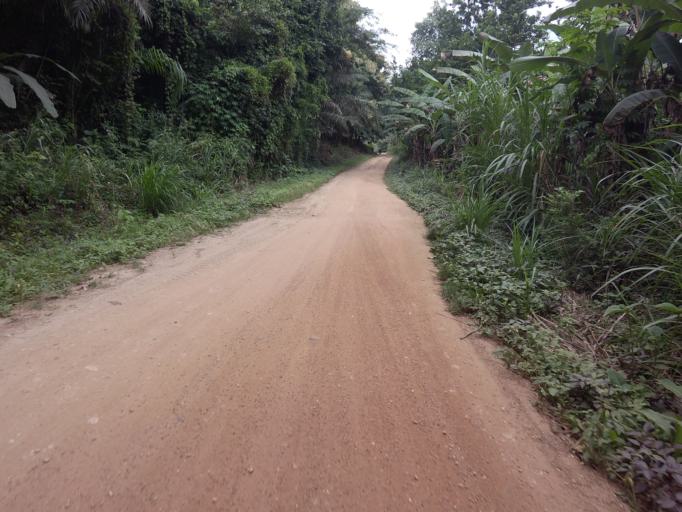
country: GH
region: Volta
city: Kpandu
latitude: 6.8788
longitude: 0.4407
